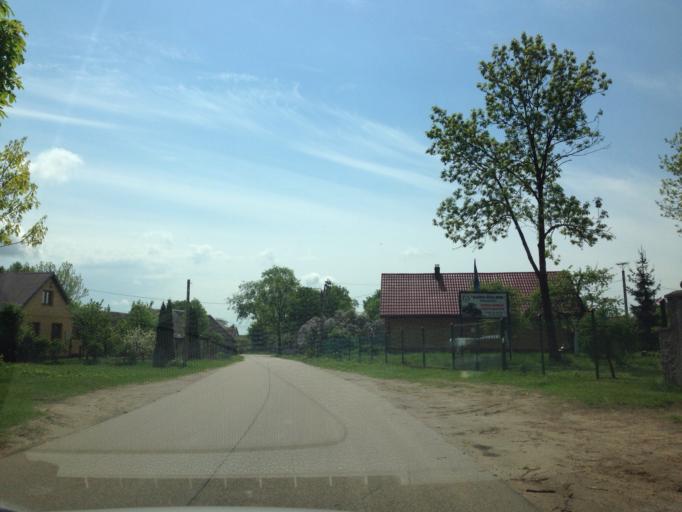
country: PL
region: Podlasie
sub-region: Powiat lomzynski
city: Wizna
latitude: 53.2796
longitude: 22.4528
